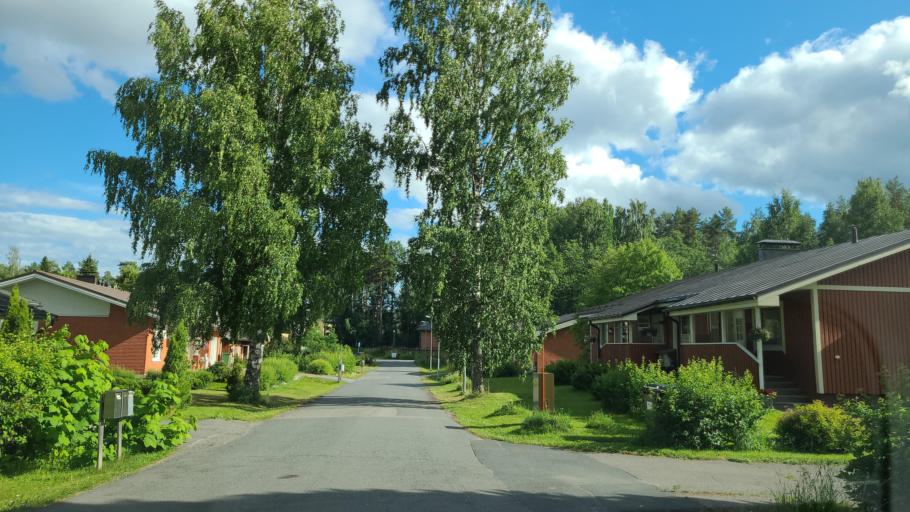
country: FI
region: Northern Savo
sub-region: Kuopio
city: Kuopio
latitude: 62.9271
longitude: 27.6266
